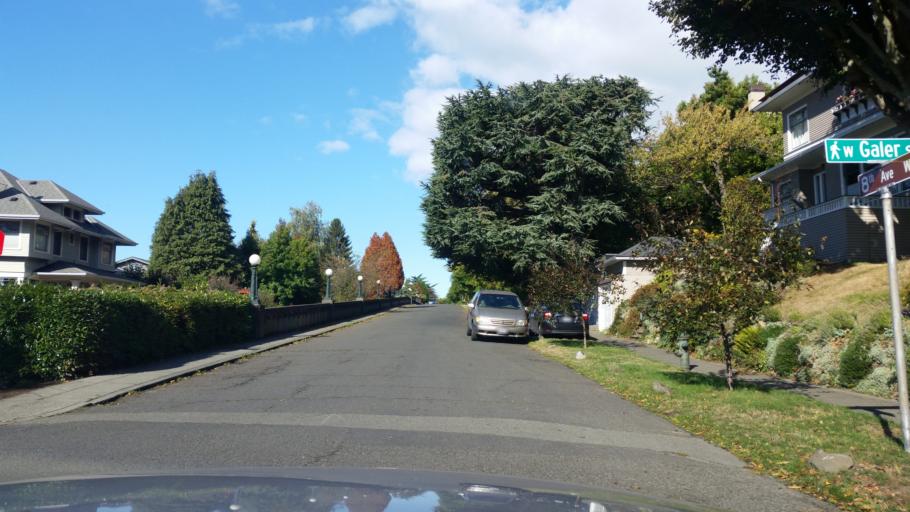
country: US
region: Washington
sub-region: King County
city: Seattle
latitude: 47.6323
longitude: -122.3677
